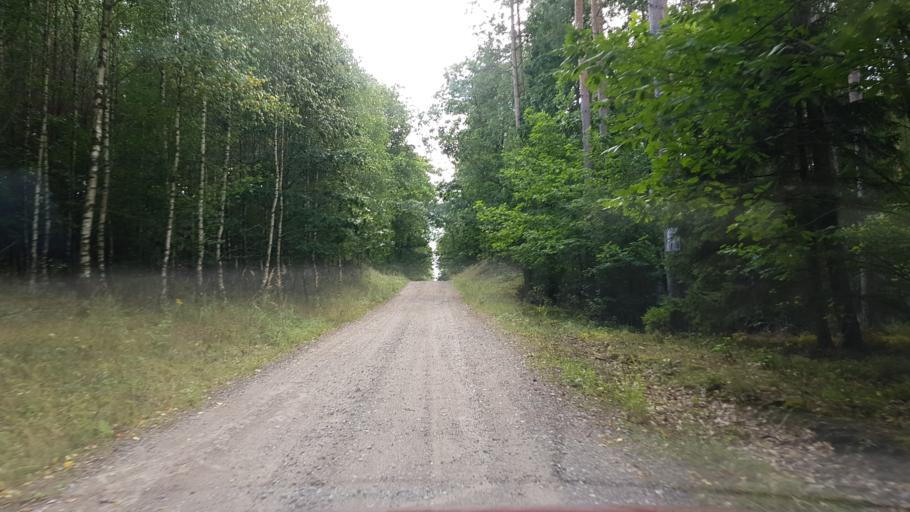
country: PL
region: West Pomeranian Voivodeship
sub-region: Powiat bialogardzki
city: Tychowo
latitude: 54.0066
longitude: 16.3024
